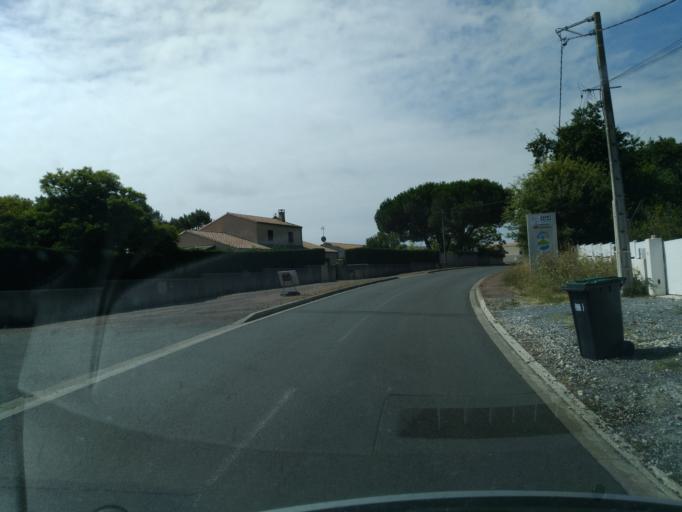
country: FR
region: Poitou-Charentes
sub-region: Departement de la Charente-Maritime
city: Vaux-sur-Mer
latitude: 45.6623
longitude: -1.0719
